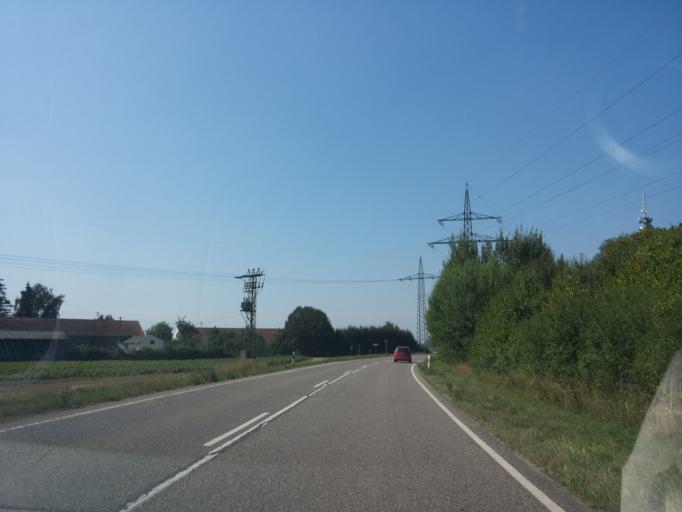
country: DE
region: Bavaria
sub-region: Upper Bavaria
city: Grossmehring
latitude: 48.7862
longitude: 11.5126
